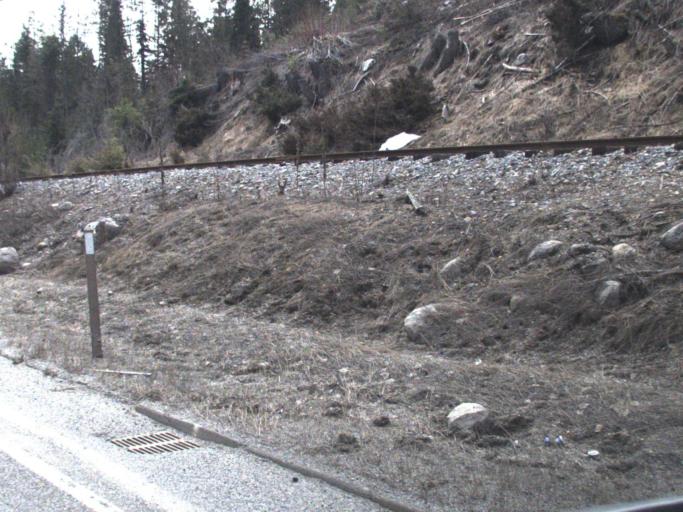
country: US
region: Washington
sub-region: Pend Oreille County
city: Newport
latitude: 48.5196
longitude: -117.2923
